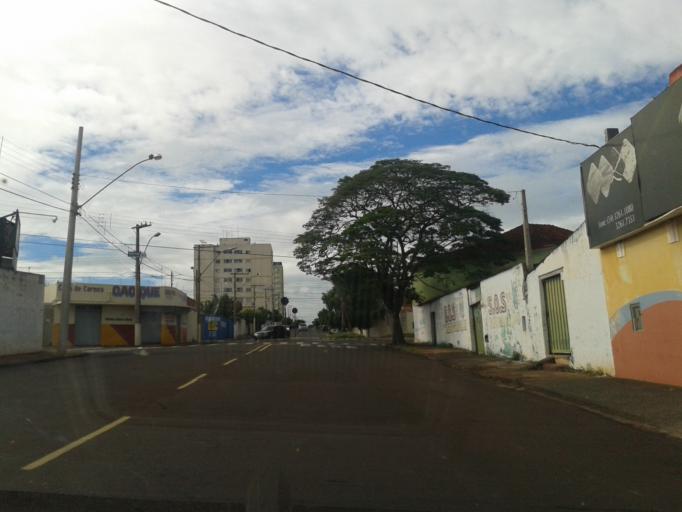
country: BR
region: Minas Gerais
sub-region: Ituiutaba
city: Ituiutaba
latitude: -18.9765
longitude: -49.4670
